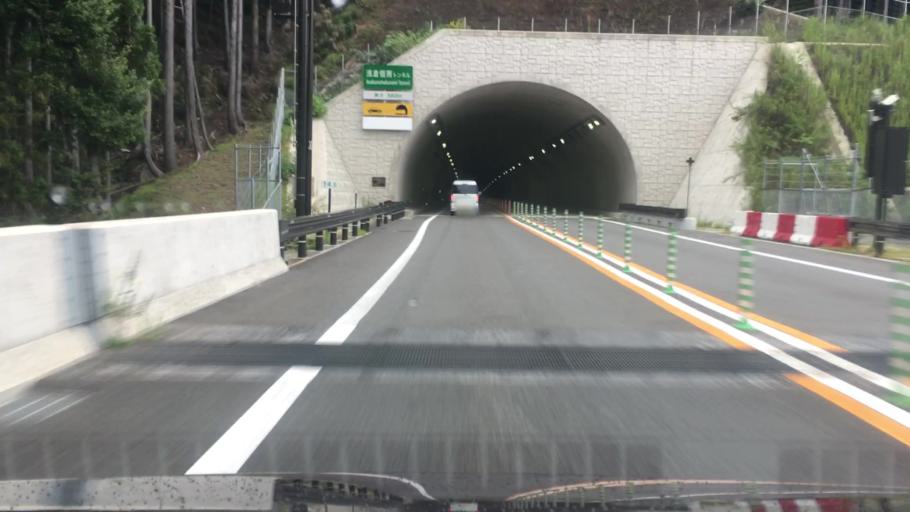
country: JP
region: Hyogo
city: Toyooka
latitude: 35.4427
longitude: 134.7671
